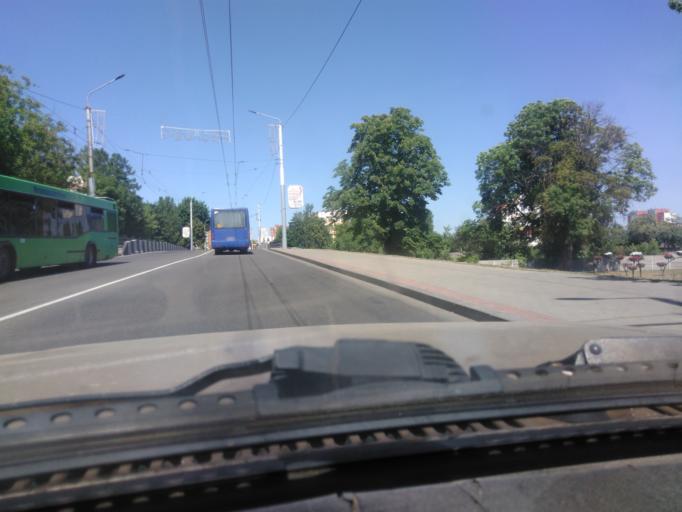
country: BY
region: Mogilev
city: Mahilyow
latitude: 53.9189
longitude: 30.3427
